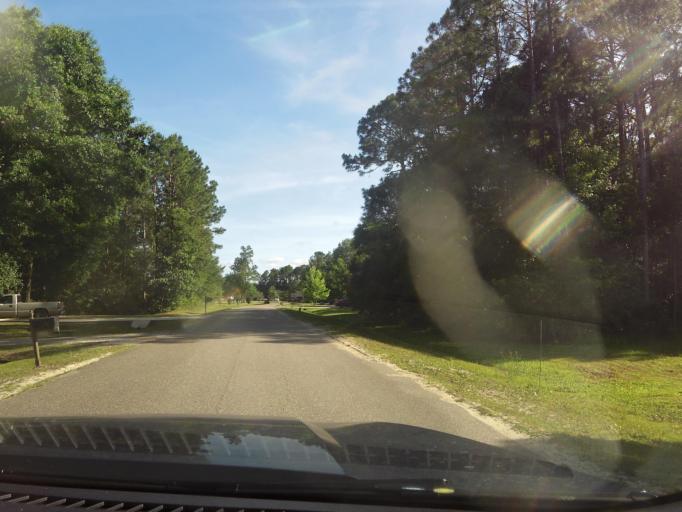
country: US
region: Florida
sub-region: Nassau County
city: Callahan
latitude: 30.5673
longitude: -81.7750
